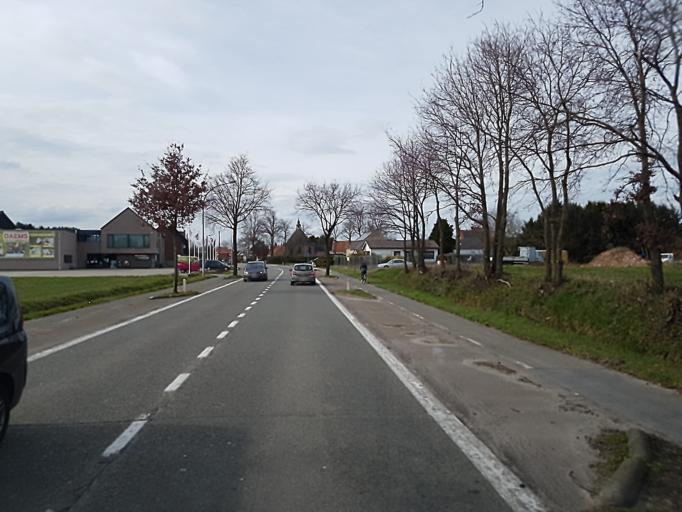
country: BE
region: Flanders
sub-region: Provincie Antwerpen
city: Retie
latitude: 51.2566
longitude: 5.1015
